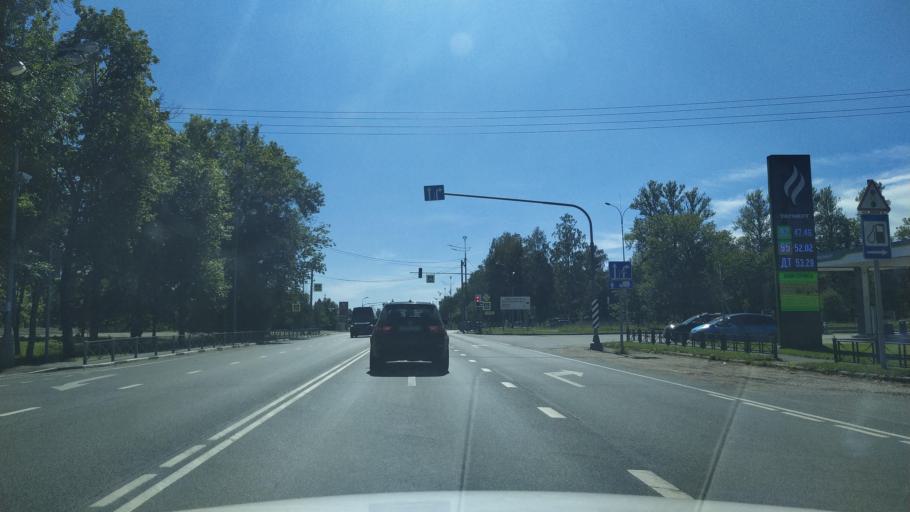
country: RU
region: Pskov
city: Pskov
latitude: 57.7958
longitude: 28.4176
